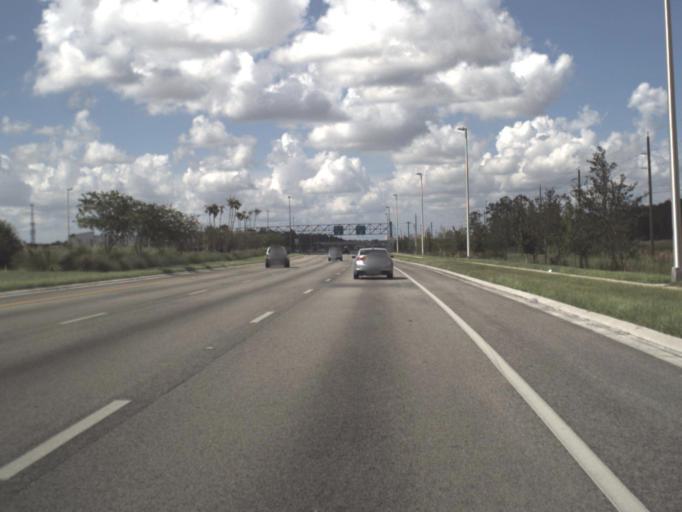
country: US
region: Florida
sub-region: Lee County
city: Tice
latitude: 26.6325
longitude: -81.7942
